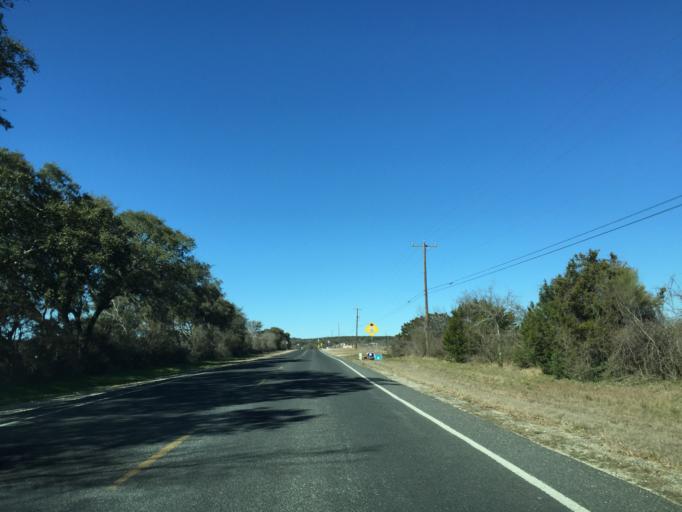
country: US
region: Texas
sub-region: Comal County
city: Bulverde
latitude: 29.7433
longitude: -98.4059
